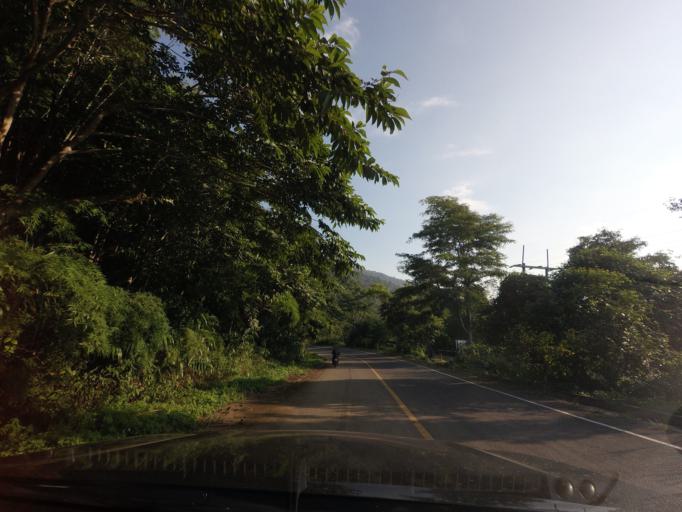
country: TH
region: Nan
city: Na Noi
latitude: 18.3691
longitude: 100.8285
